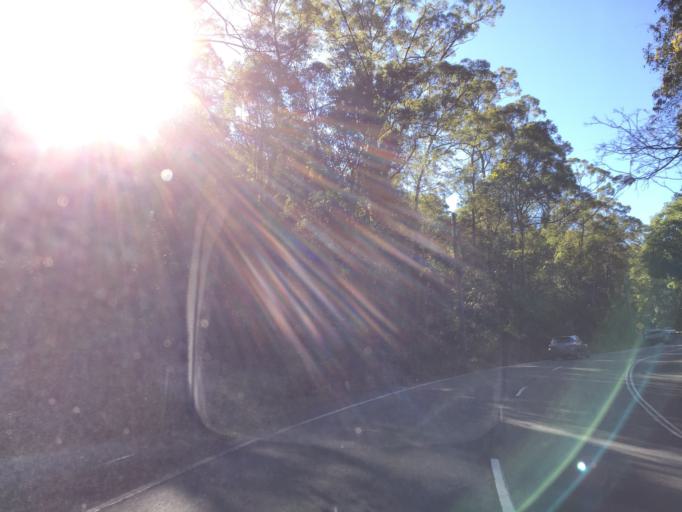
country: AU
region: Queensland
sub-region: Moreton Bay
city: Ferny Hills
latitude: -27.4275
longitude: 152.9430
